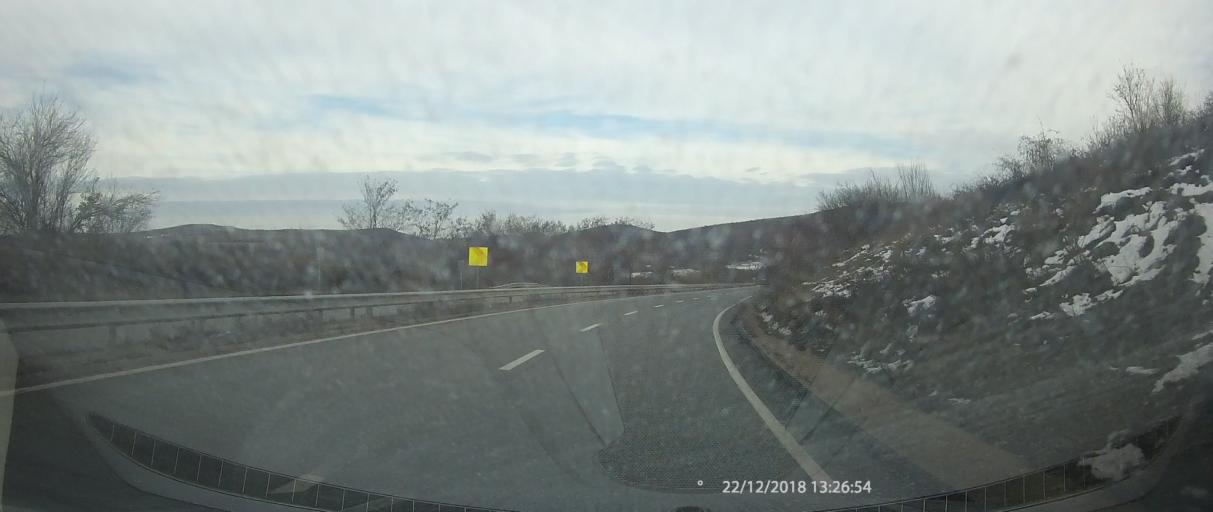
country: BG
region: Lovech
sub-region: Obshtina Yablanitsa
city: Yablanitsa
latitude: 43.0498
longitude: 24.1259
